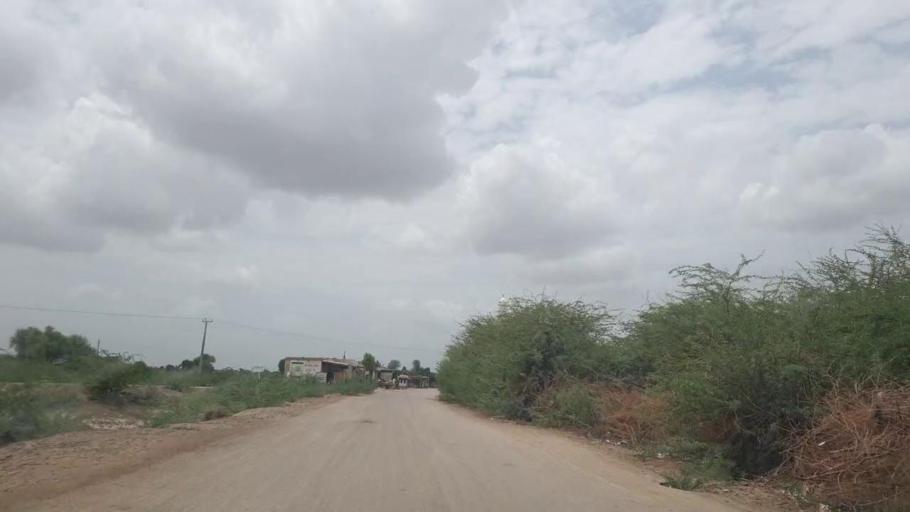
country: PK
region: Sindh
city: Naukot
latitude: 24.9161
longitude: 69.2717
